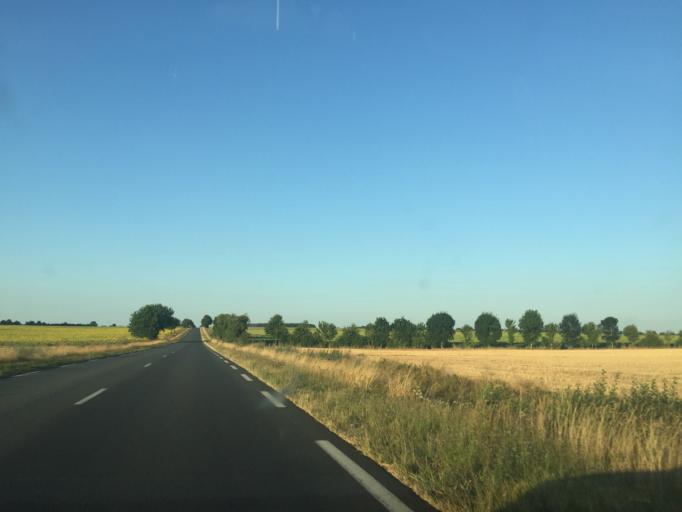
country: FR
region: Poitou-Charentes
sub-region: Departement des Deux-Sevres
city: Pamproux
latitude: 46.3442
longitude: -0.0098
